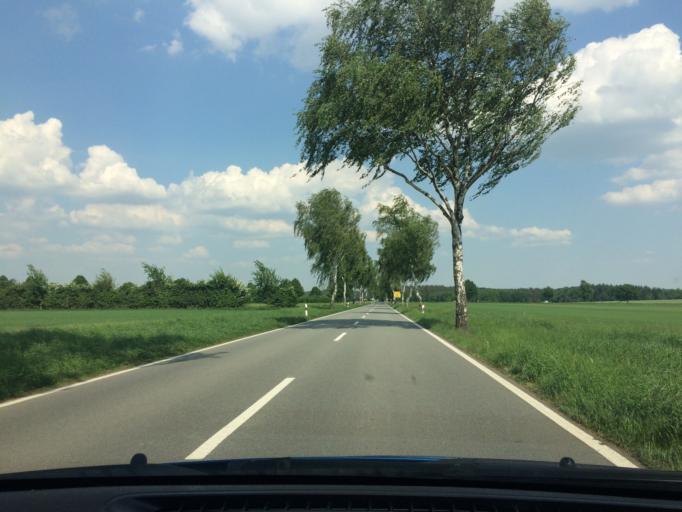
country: DE
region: Lower Saxony
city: Tosterglope
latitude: 53.2119
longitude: 10.8344
